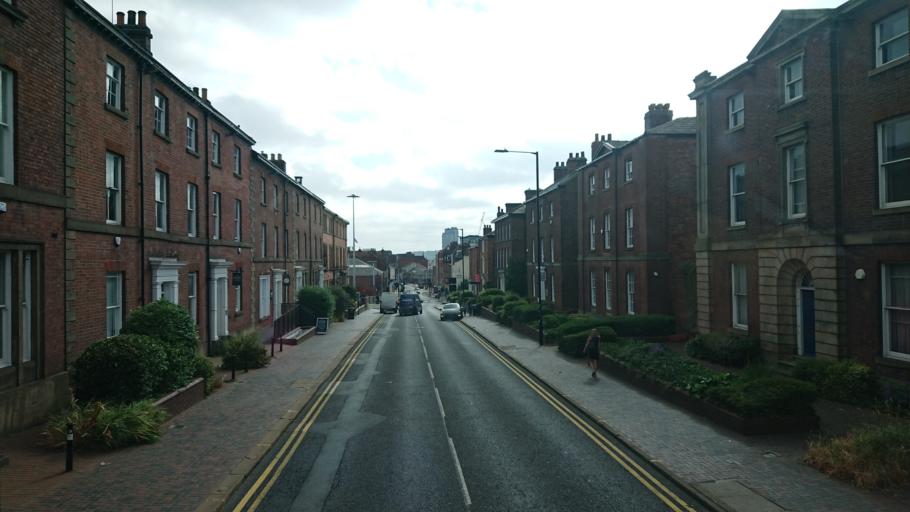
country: GB
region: England
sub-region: Sheffield
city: Sheffield
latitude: 53.3803
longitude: -1.4861
